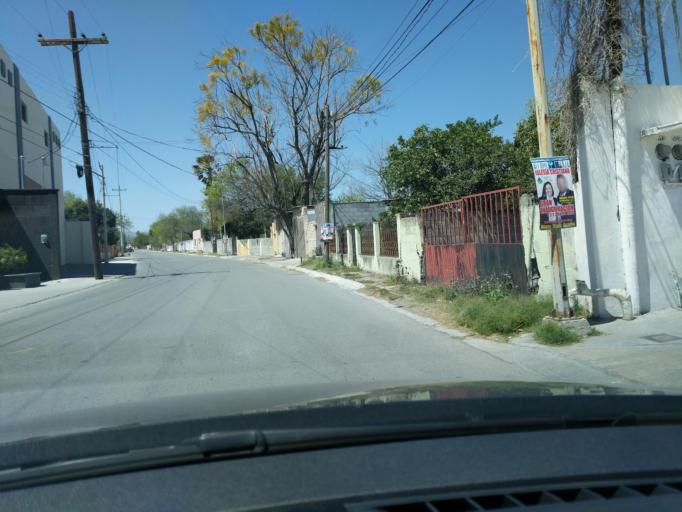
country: MX
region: Nuevo Leon
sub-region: Apodaca
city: Artemio Trevino
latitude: 25.8131
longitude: -100.1401
